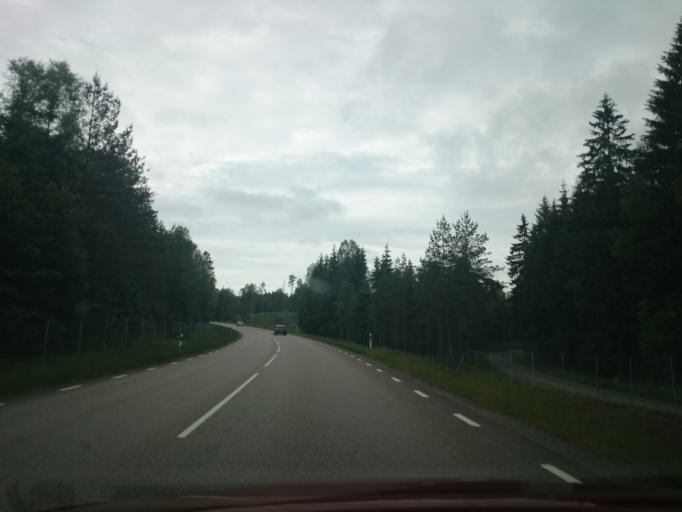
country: SE
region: Vaestra Goetaland
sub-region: Harryda Kommun
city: Hindas
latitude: 57.6936
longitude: 12.3762
